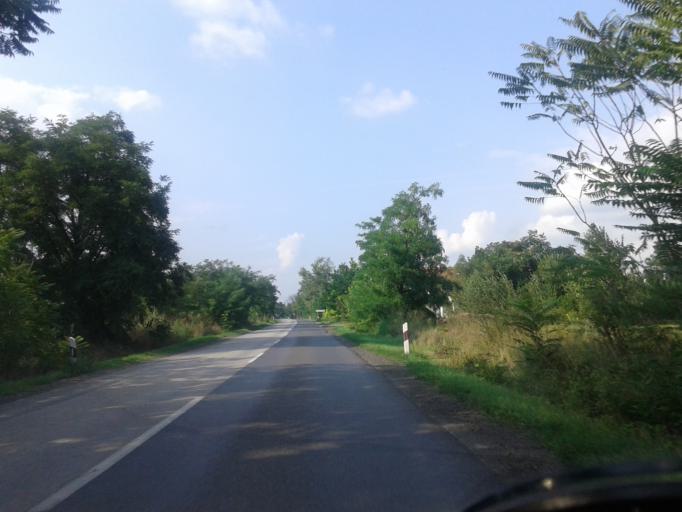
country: HU
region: Bacs-Kiskun
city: Szalkszentmarton
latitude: 46.9534
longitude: 18.9792
